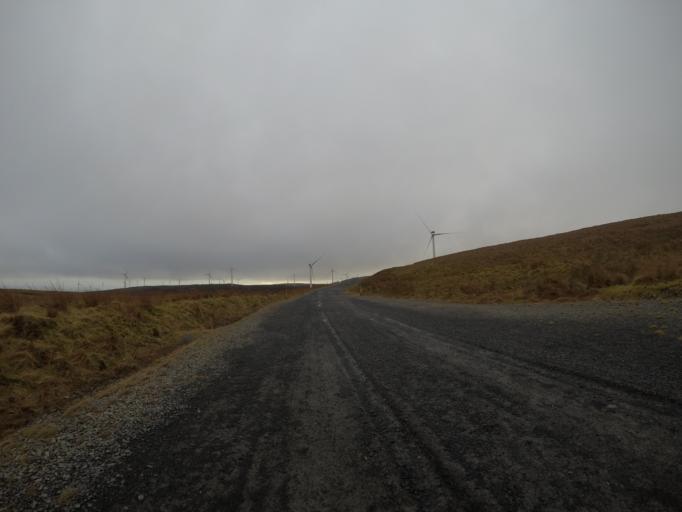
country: GB
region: Scotland
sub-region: North Ayrshire
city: Fairlie
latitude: 55.7605
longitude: -4.7918
